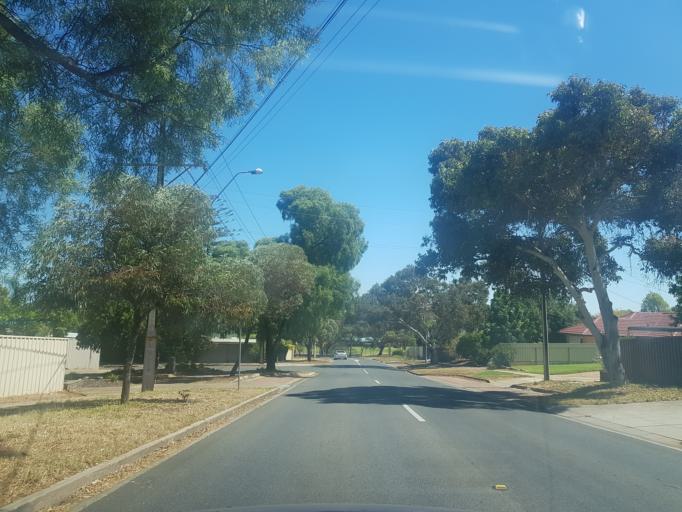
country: AU
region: South Australia
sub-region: Salisbury
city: Ingle Farm
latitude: -34.8147
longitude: 138.6533
